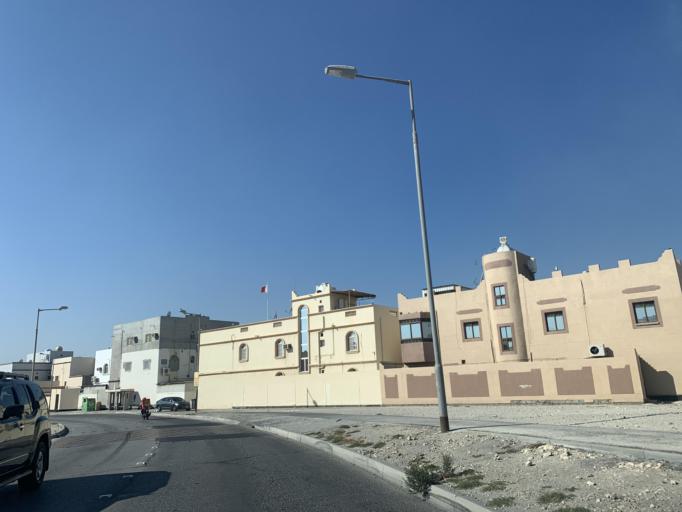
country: BH
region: Central Governorate
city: Madinat Hamad
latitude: 26.1165
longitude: 50.5064
